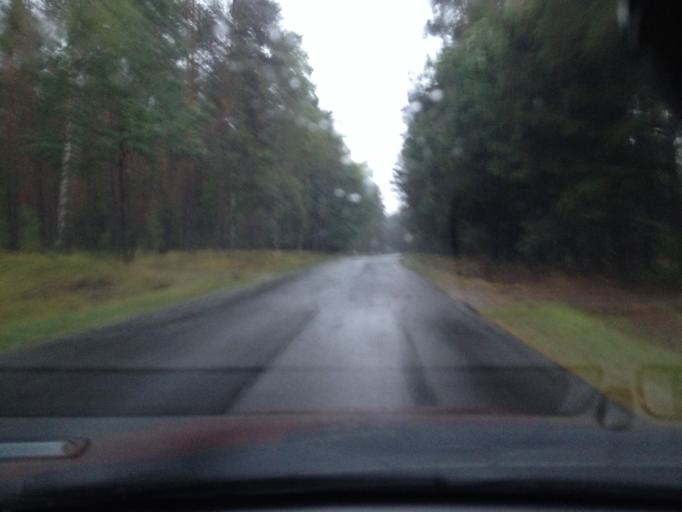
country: PL
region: Lubusz
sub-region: Powiat zaganski
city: Gozdnica
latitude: 51.3503
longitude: 15.1284
